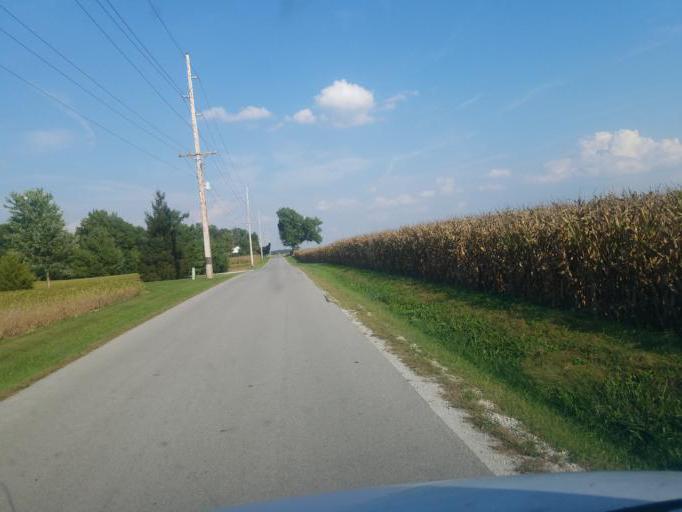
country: US
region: Ohio
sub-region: Wyandot County
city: Carey
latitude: 40.9237
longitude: -83.3098
